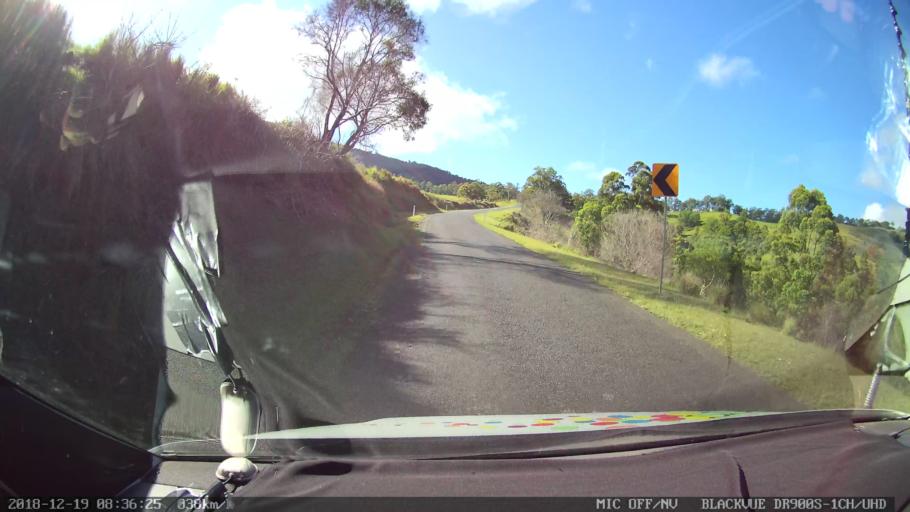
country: AU
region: New South Wales
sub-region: Kyogle
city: Kyogle
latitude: -28.3257
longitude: 152.9730
